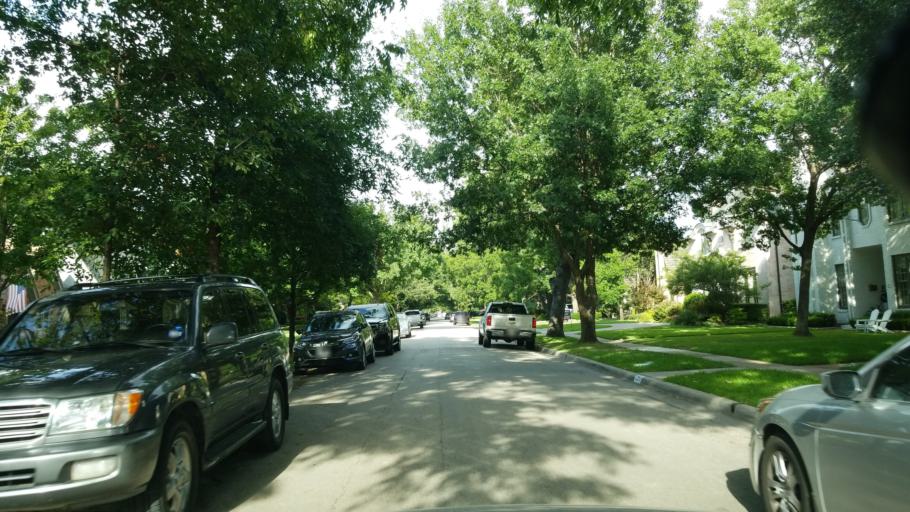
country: US
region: Texas
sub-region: Dallas County
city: University Park
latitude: 32.8530
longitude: -96.7858
